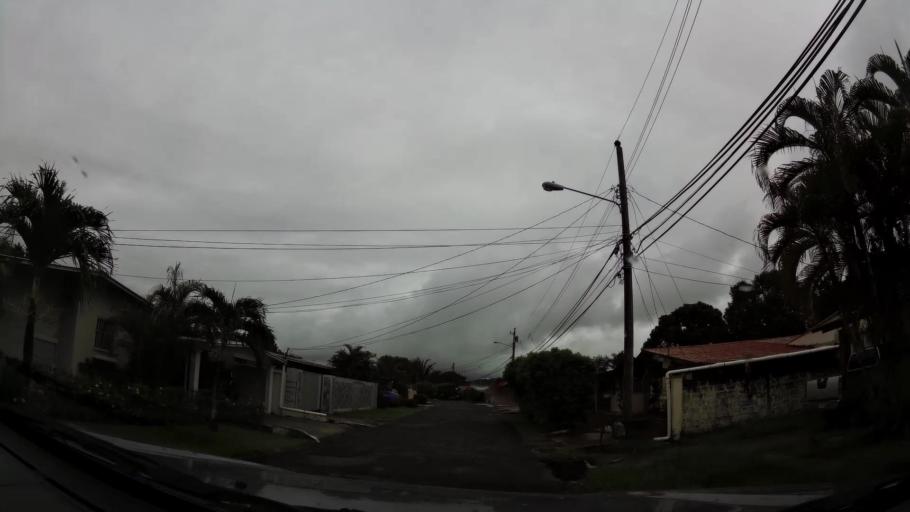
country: PA
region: Chiriqui
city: David
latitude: 8.4347
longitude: -82.4449
